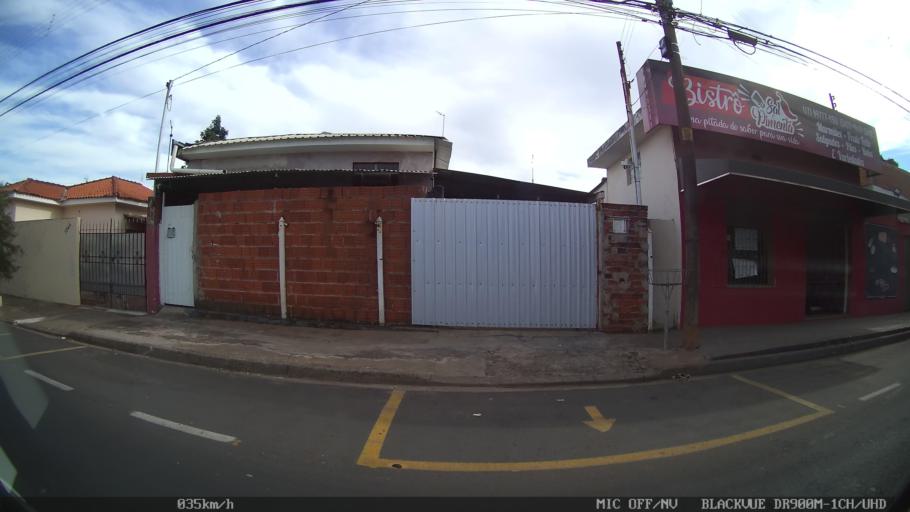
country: BR
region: Sao Paulo
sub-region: Catanduva
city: Catanduva
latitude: -21.1386
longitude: -48.9990
